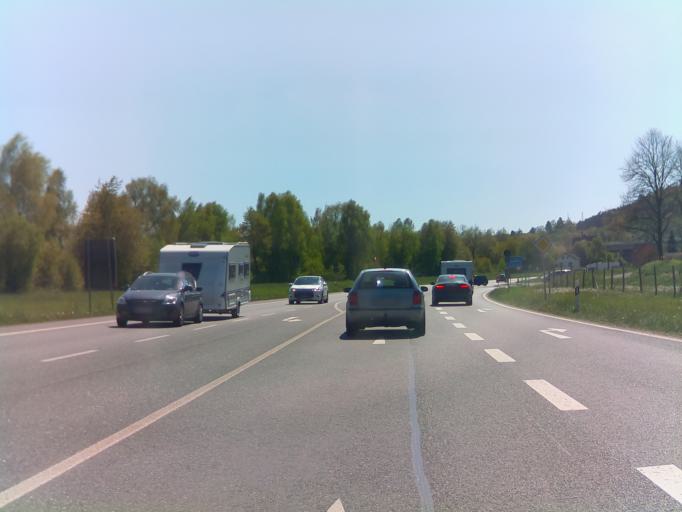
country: DE
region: Hesse
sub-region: Regierungsbezirk Kassel
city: Niederaula
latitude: 50.7803
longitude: 9.5903
